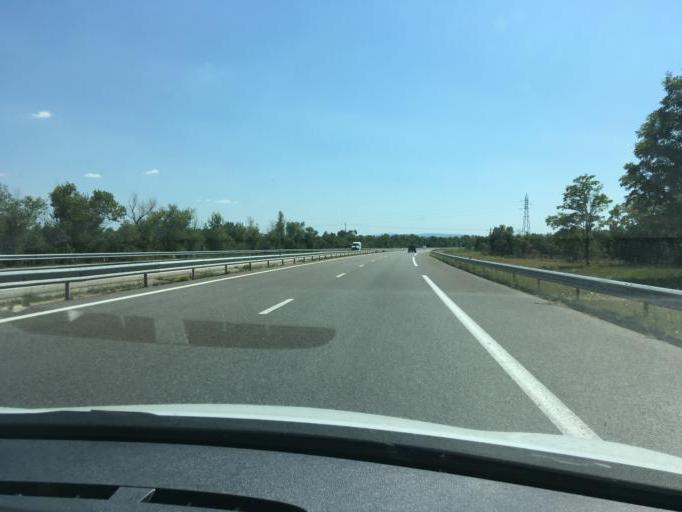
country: FR
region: Provence-Alpes-Cote d'Azur
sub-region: Departement des Alpes-de-Haute-Provence
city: Sainte-Tulle
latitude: 43.7787
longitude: 5.8021
